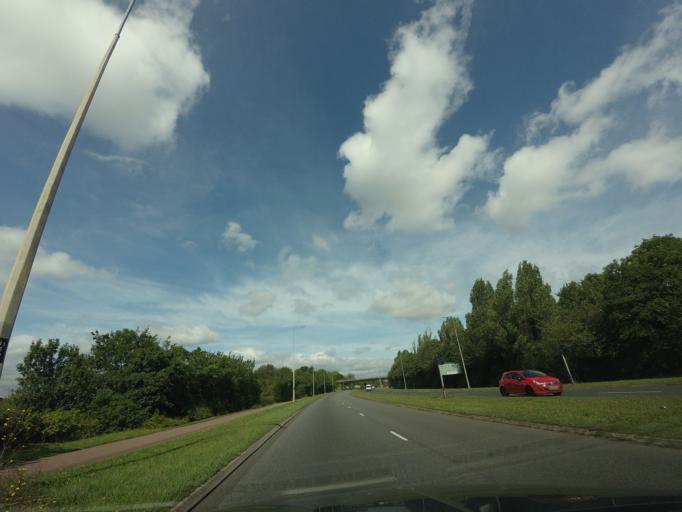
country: GB
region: England
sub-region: Milton Keynes
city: Wavendon
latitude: 52.0191
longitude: -0.6856
